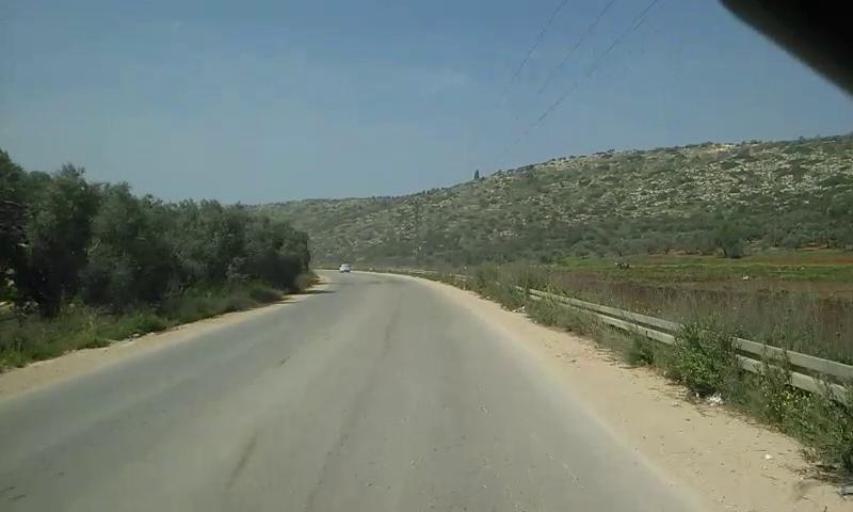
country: PS
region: West Bank
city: Az Zababidah
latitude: 32.4072
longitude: 35.3091
